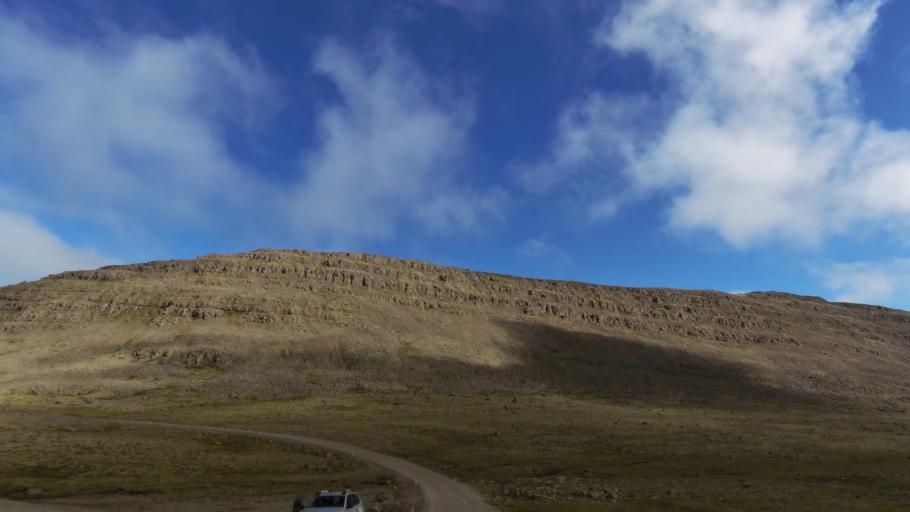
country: IS
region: West
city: Olafsvik
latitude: 65.5766
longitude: -24.0846
